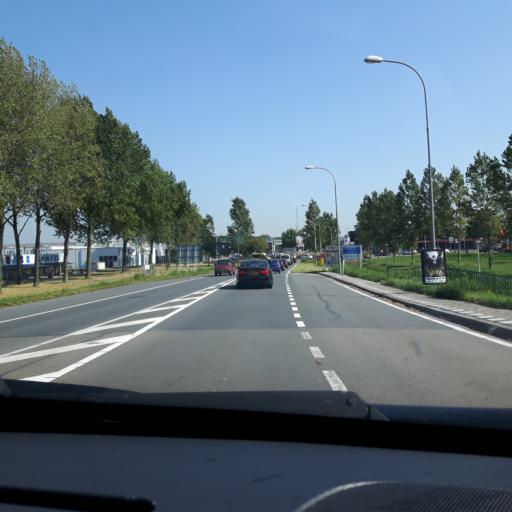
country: NL
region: Zeeland
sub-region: Gemeente Goes
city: Goes
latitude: 51.4926
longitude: 3.8745
